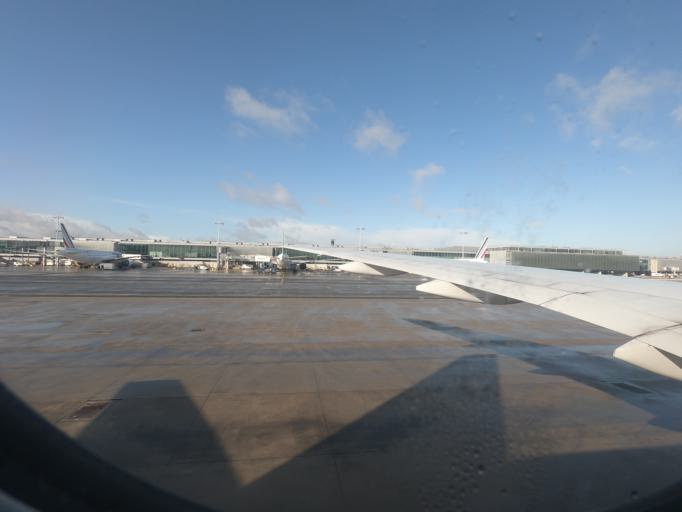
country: FR
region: Ile-de-France
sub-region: Departement de Seine-et-Marne
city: Mitry-Mory
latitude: 49.0030
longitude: 2.5887
